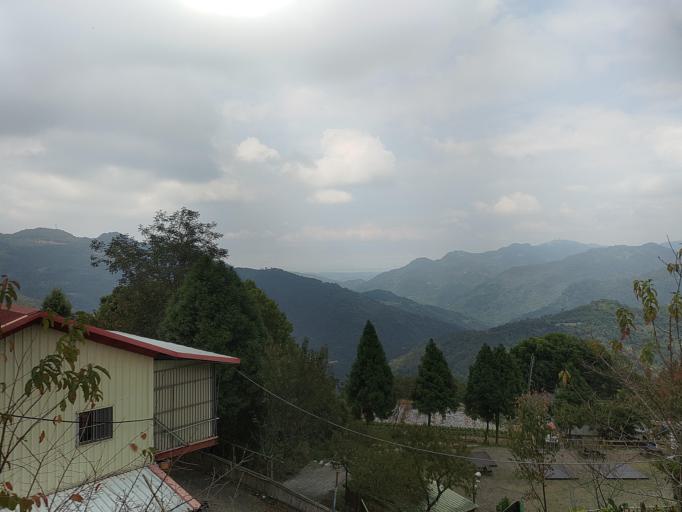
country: TW
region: Taiwan
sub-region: Hsinchu
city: Hsinchu
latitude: 24.6093
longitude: 121.1000
